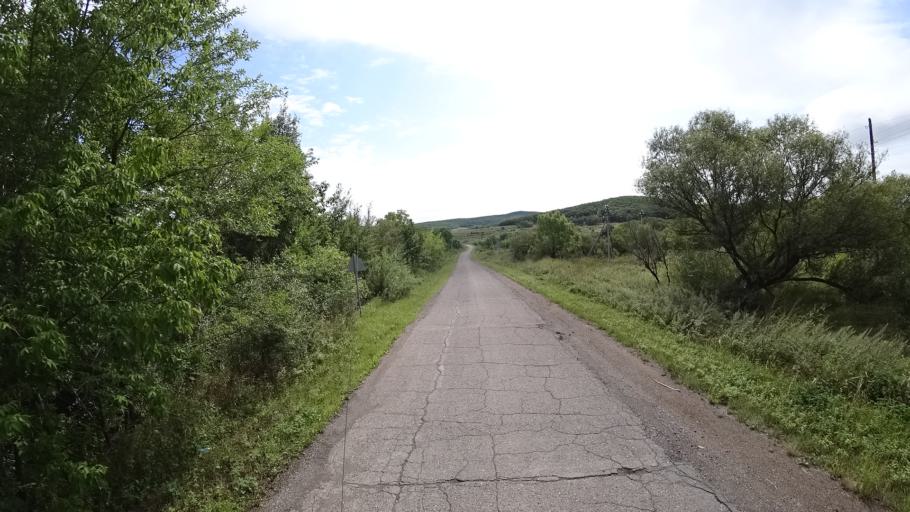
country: RU
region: Primorskiy
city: Lyalichi
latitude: 44.1401
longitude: 132.3882
